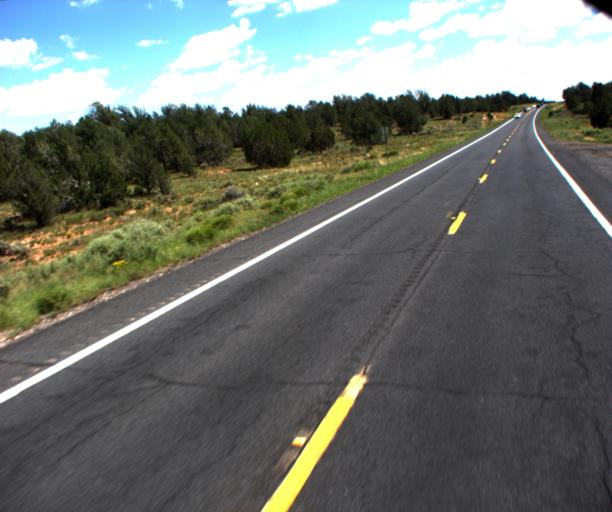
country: US
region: Arizona
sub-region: Coconino County
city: Grand Canyon Village
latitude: 35.8417
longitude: -112.1322
